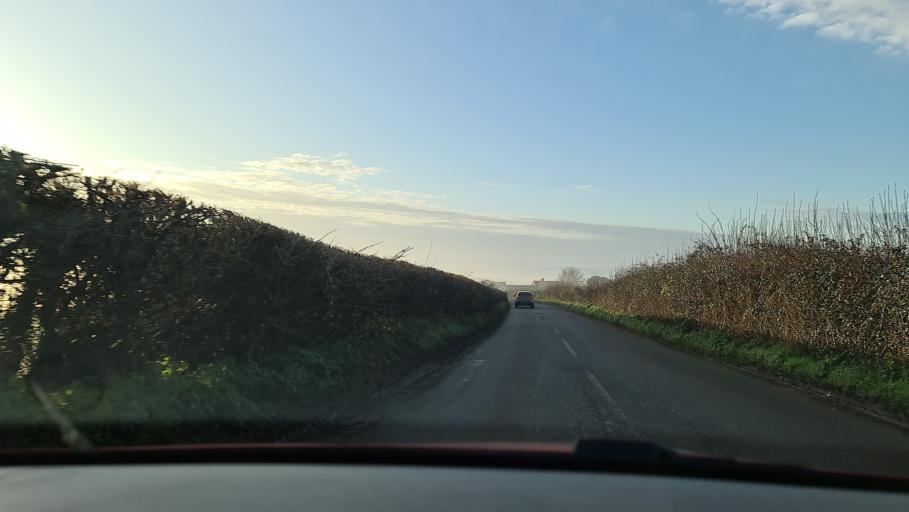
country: GB
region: England
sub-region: Buckinghamshire
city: Long Crendon
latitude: 51.8191
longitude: -0.9808
